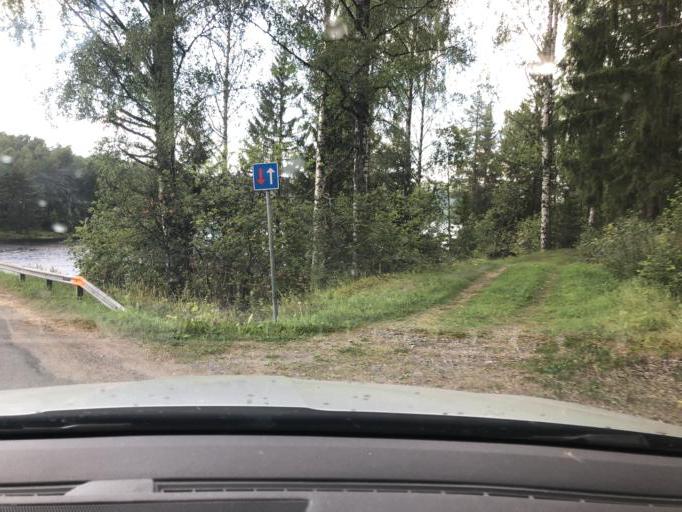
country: SE
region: Vaesternorrland
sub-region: Solleftea Kommun
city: Solleftea
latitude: 63.2471
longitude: 17.1984
